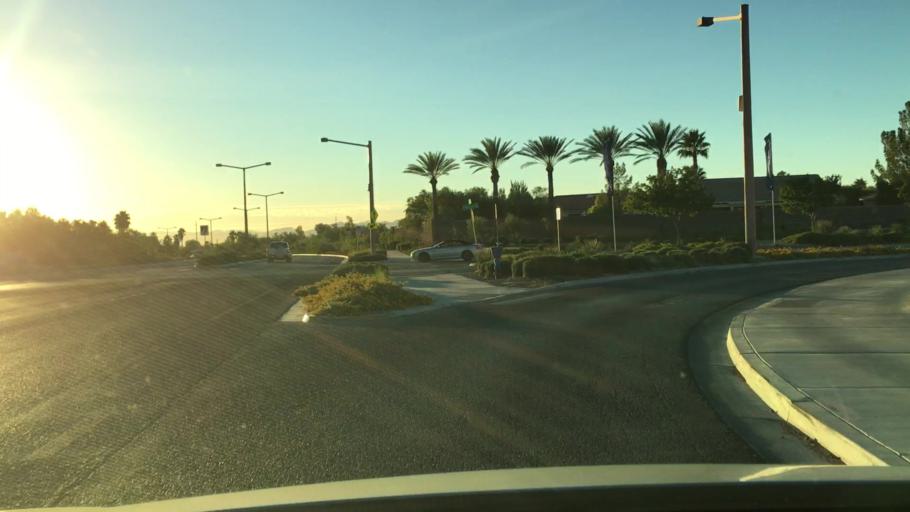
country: US
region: Nevada
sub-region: Clark County
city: Summerlin South
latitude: 36.1002
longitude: -115.3250
